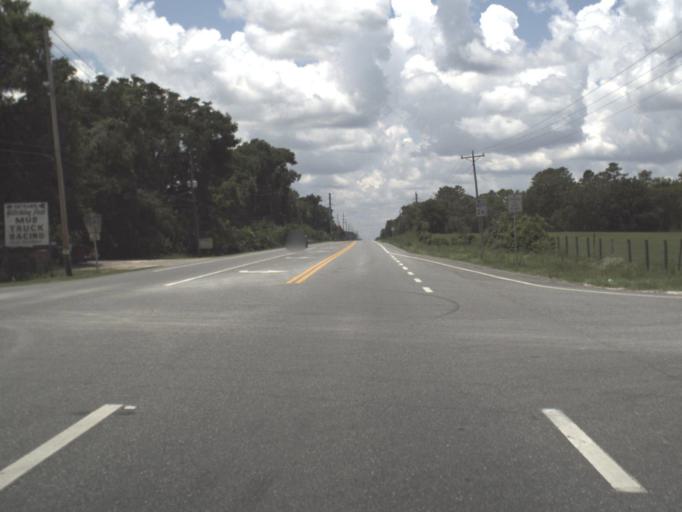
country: US
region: Florida
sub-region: Alachua County
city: Newberry
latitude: 29.6389
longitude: -82.6734
